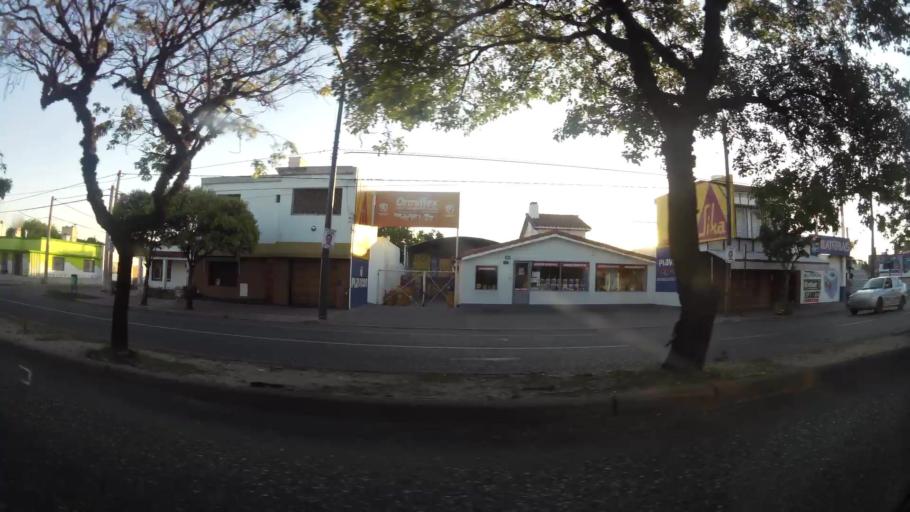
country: AR
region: Cordoba
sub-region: Departamento de Capital
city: Cordoba
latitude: -31.3849
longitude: -64.2202
